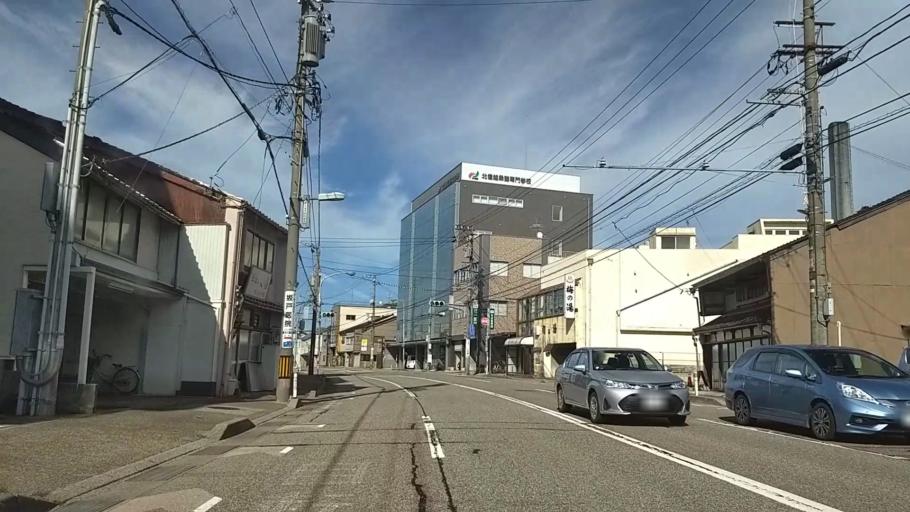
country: JP
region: Ishikawa
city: Kanazawa-shi
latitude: 36.5777
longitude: 136.6690
